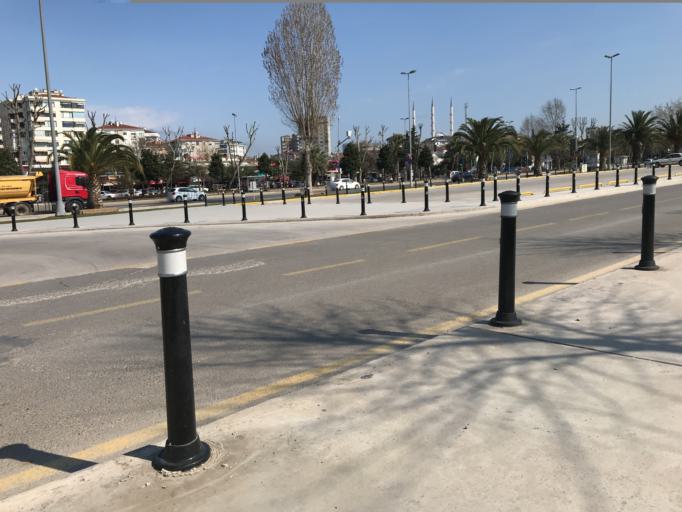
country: TR
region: Istanbul
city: Maltepe
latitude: 40.9268
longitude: 29.1218
